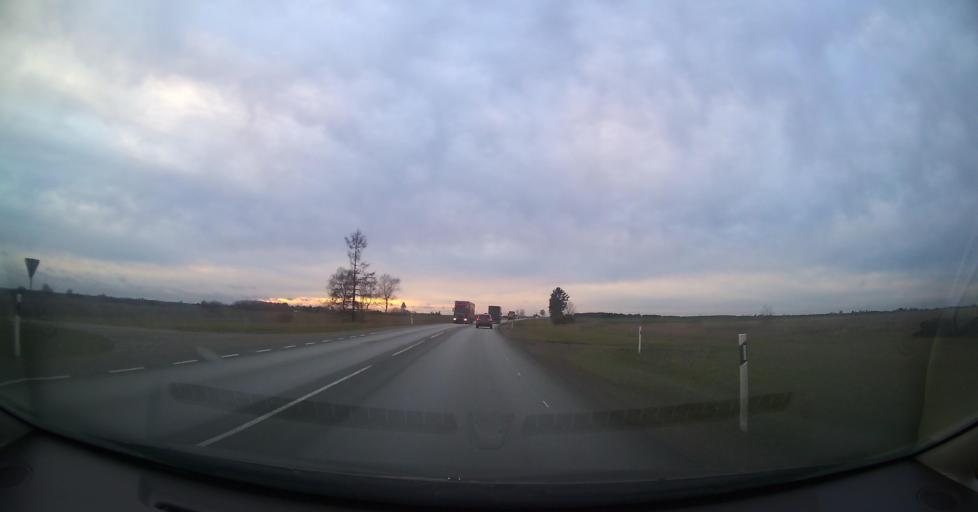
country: EE
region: Ida-Virumaa
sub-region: Puessi linn
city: Pussi
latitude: 59.4038
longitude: 27.0911
